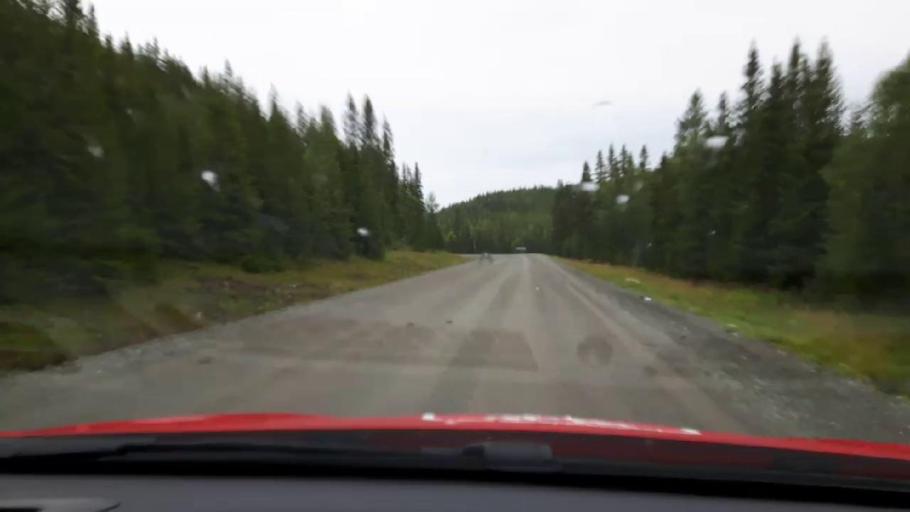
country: SE
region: Jaemtland
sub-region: Are Kommun
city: Are
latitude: 63.4245
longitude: 12.7411
